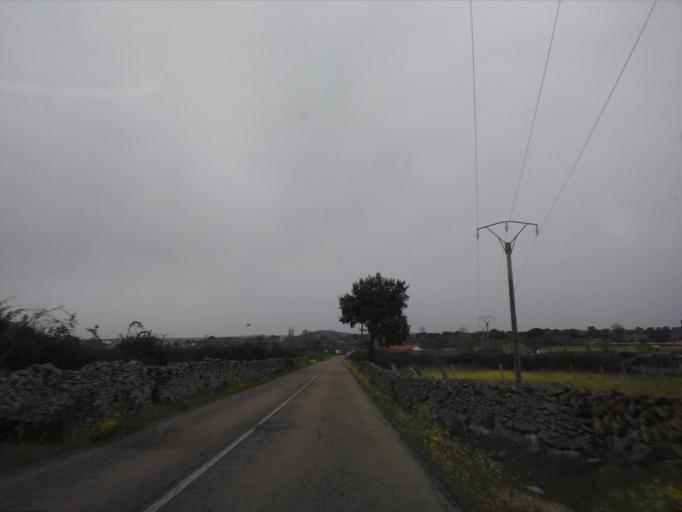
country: ES
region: Castille and Leon
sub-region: Provincia de Salamanca
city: Yecla de Yeltes
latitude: 40.9637
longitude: -6.4869
